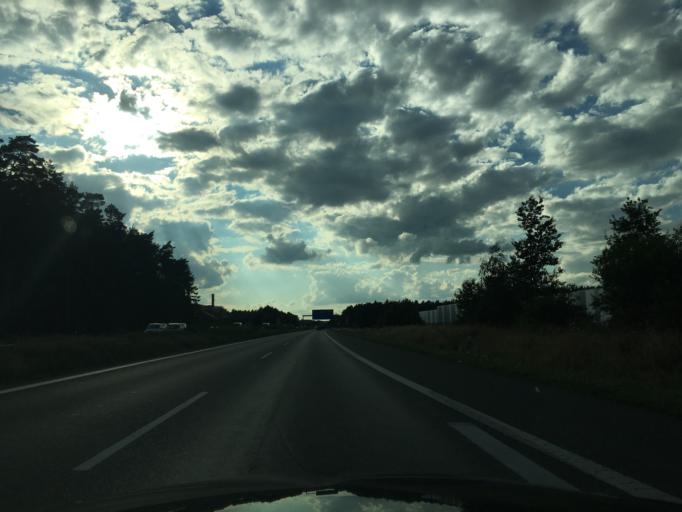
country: DE
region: Bavaria
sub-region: Regierungsbezirk Mittelfranken
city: Burgoberbach
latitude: 49.2526
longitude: 10.6066
